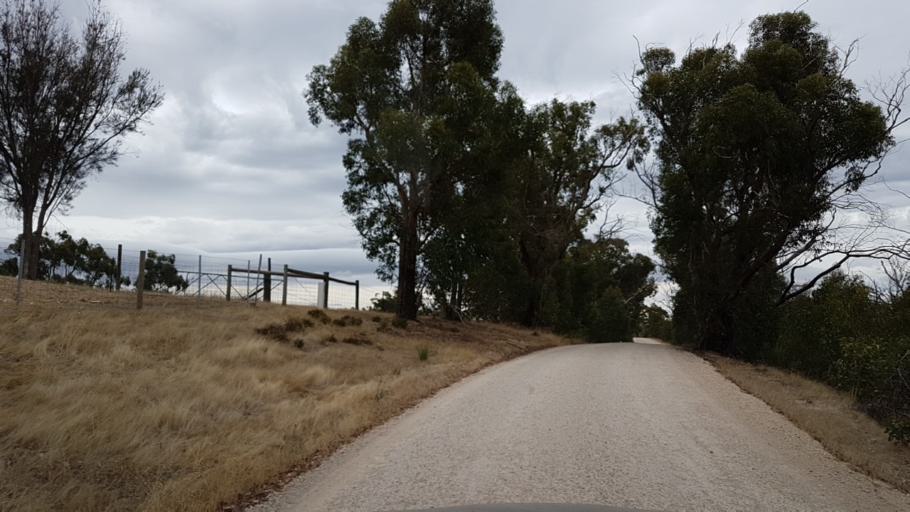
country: AU
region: South Australia
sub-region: Tea Tree Gully
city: Golden Grove
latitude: -34.7773
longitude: 138.8127
